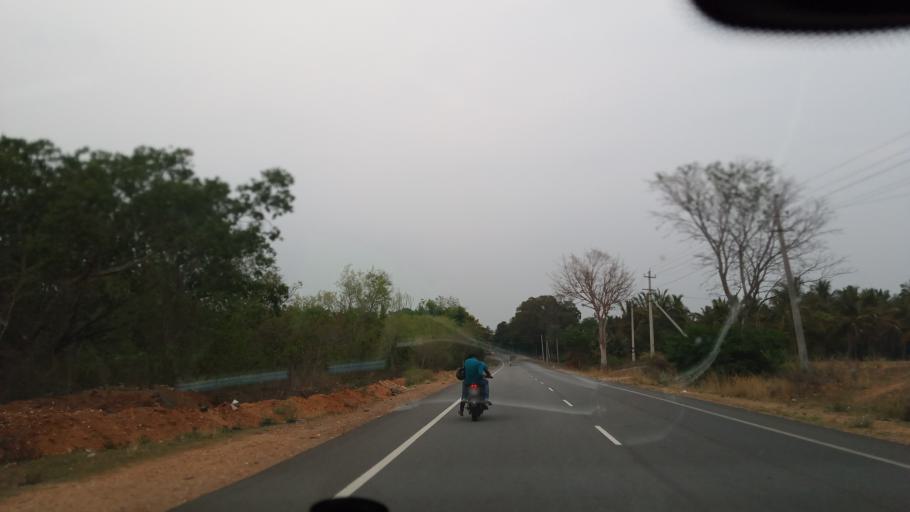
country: IN
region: Karnataka
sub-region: Mandya
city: Nagamangala
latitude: 12.7832
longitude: 76.7464
